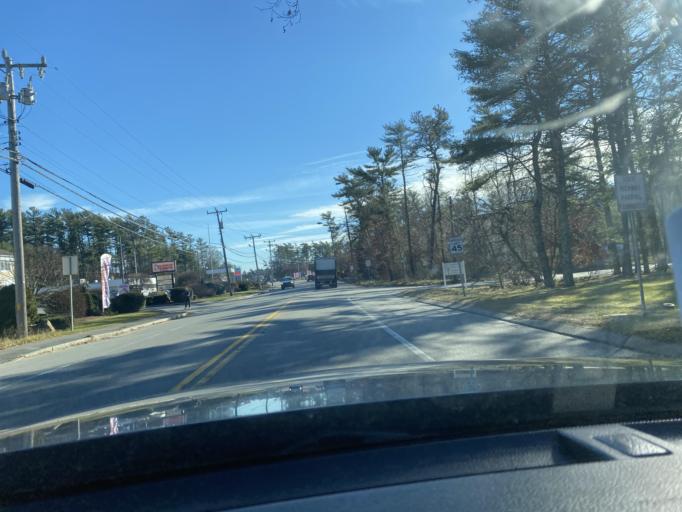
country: US
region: Massachusetts
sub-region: Plymouth County
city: West Wareham
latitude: 41.7893
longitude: -70.7514
